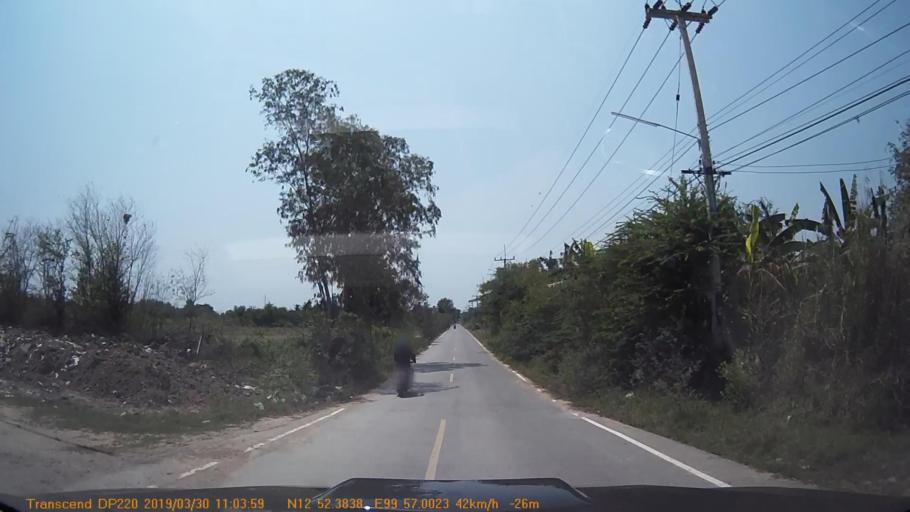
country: TH
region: Phetchaburi
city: Cha-am
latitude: 12.8730
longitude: 99.9501
